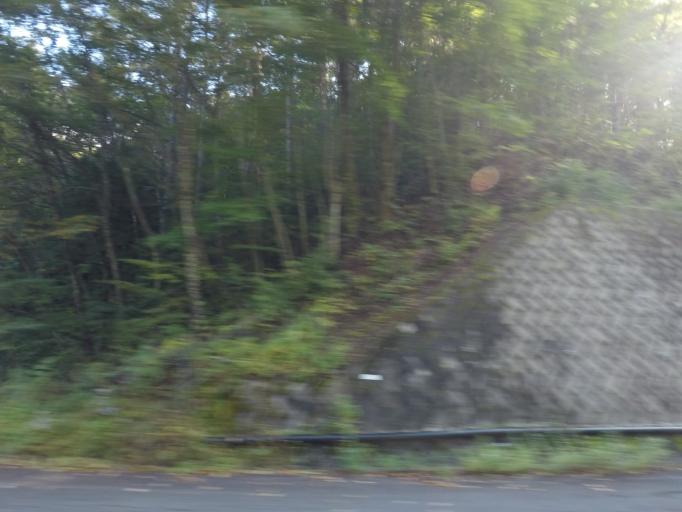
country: JP
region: Nagano
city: Ina
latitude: 35.9599
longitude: 137.7757
